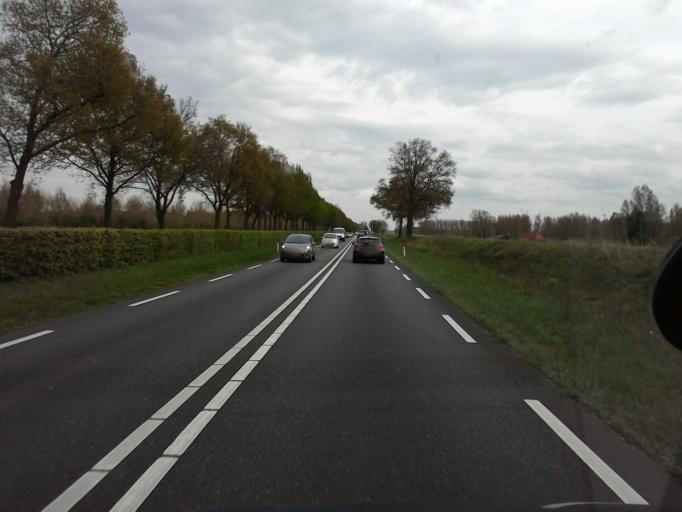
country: NL
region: North Brabant
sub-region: Gemeente Schijndel
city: Schijndel
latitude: 51.6405
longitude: 5.4727
